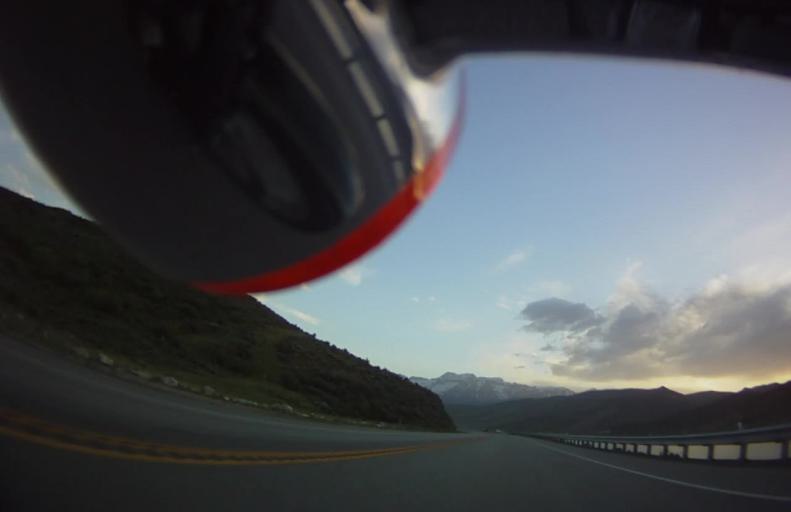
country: US
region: Utah
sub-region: Wasatch County
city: Midway
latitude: 40.4543
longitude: -111.4746
